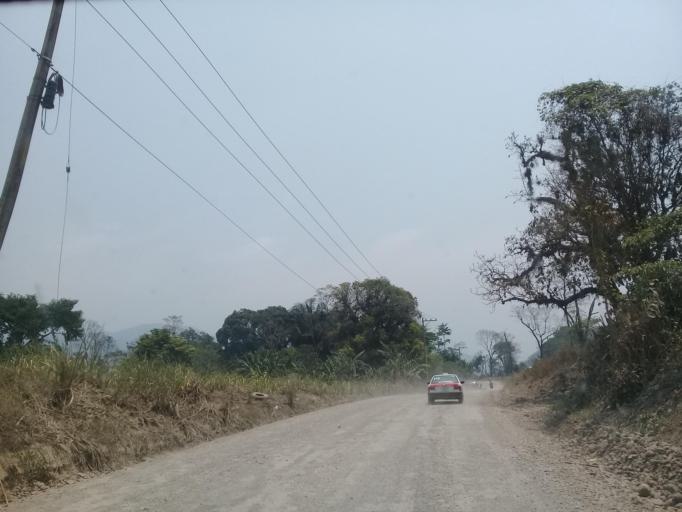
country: MX
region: Veracruz
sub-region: Tezonapa
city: Laguna Chica (Pueblo Nuevo)
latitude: 18.5647
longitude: -96.7220
